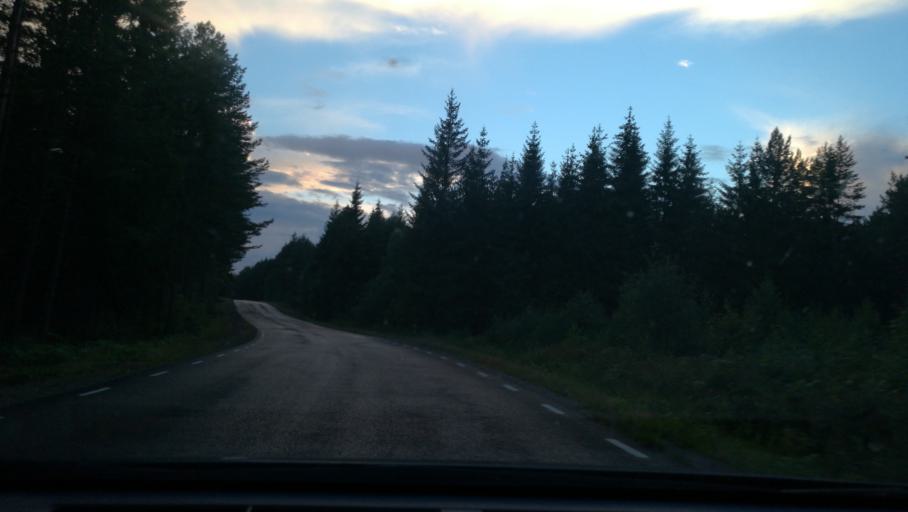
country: SE
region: OEstergoetland
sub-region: Norrkopings Kommun
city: Svartinge
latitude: 58.8203
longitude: 16.0629
